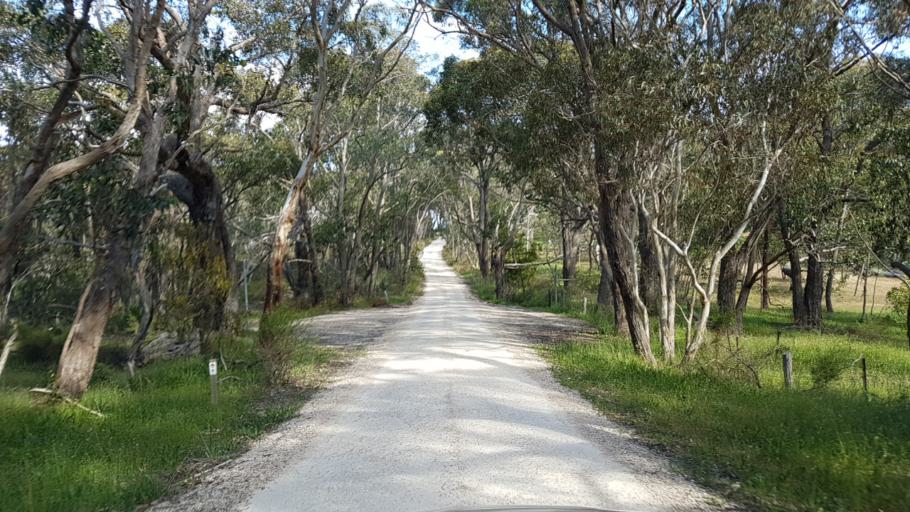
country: AU
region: South Australia
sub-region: Adelaide Hills
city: Adelaide Hills
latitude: -34.9054
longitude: 138.7357
